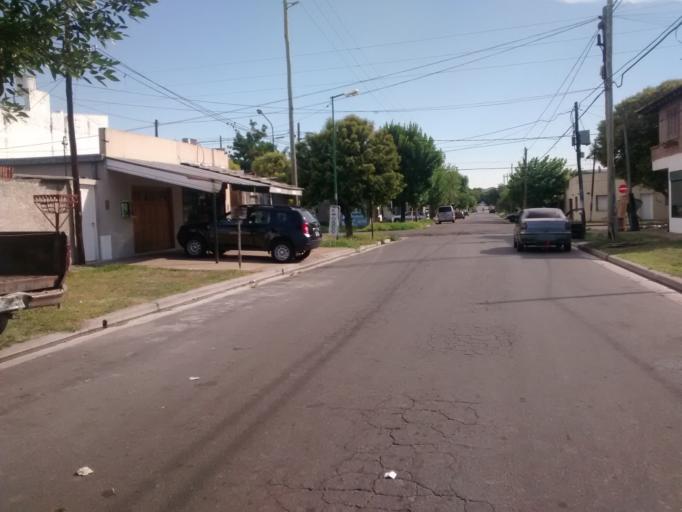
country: AR
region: Buenos Aires
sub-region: Partido de La Plata
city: La Plata
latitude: -34.9512
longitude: -57.9459
